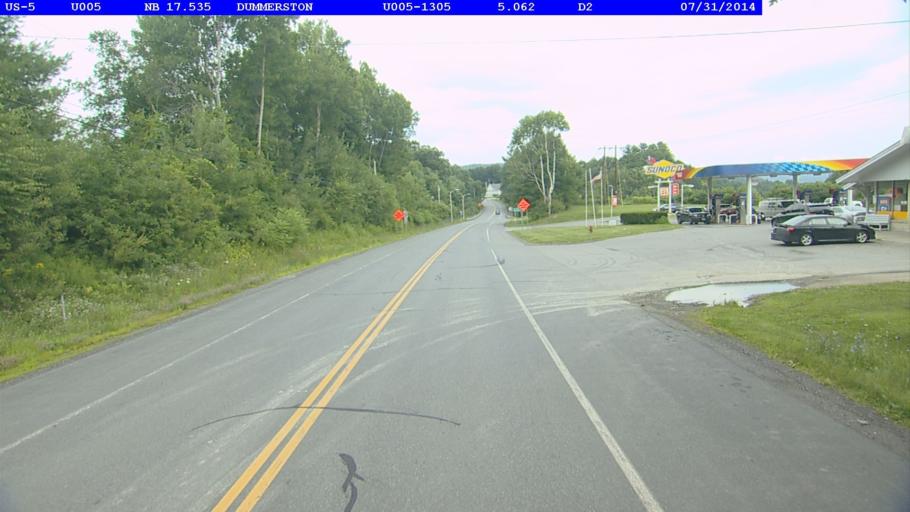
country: US
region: New Hampshire
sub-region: Cheshire County
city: Westmoreland
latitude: 42.9638
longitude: -72.5276
